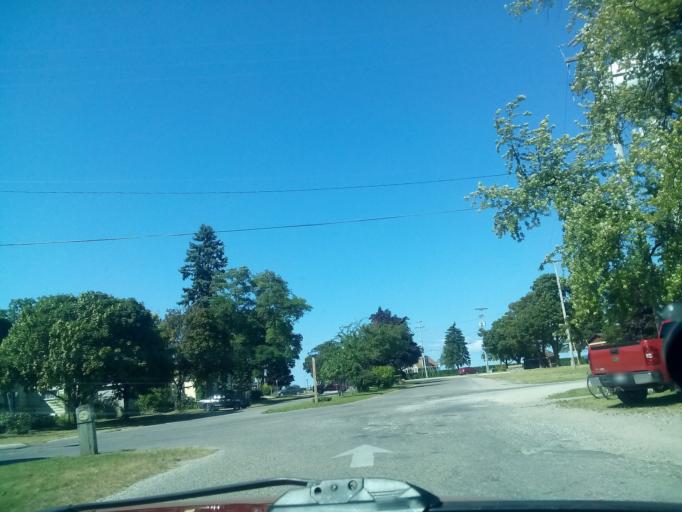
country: US
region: Michigan
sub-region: Mackinac County
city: Saint Ignace
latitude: 45.7824
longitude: -84.7245
